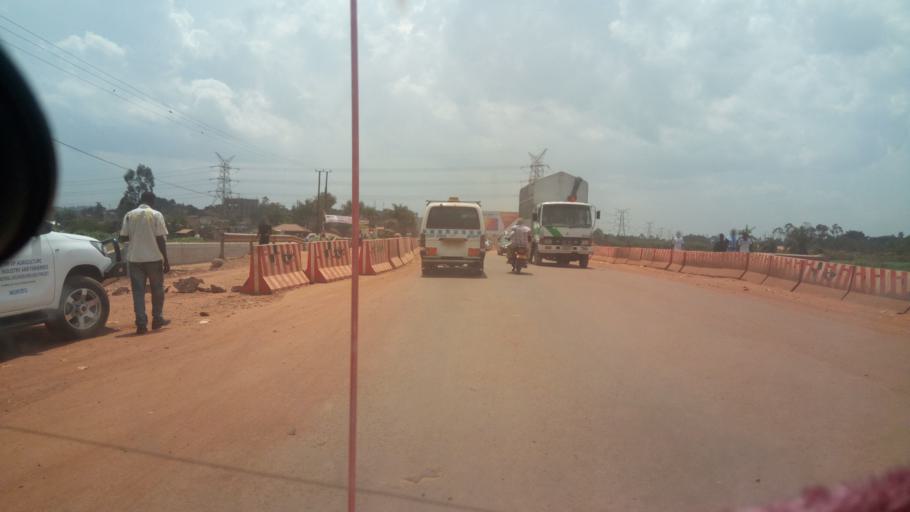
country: UG
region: Central Region
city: Kampala Central Division
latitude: 0.3463
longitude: 32.5417
